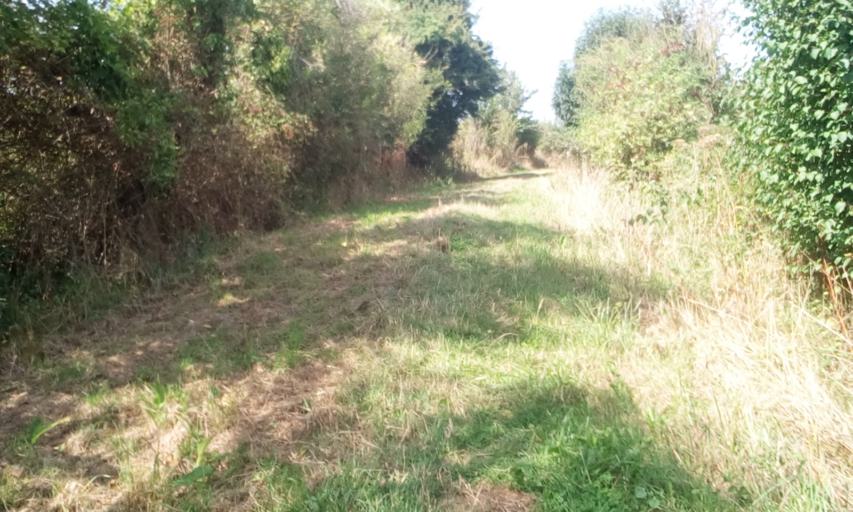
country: FR
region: Lower Normandy
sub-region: Departement du Calvados
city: Argences
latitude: 49.1457
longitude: -0.1108
